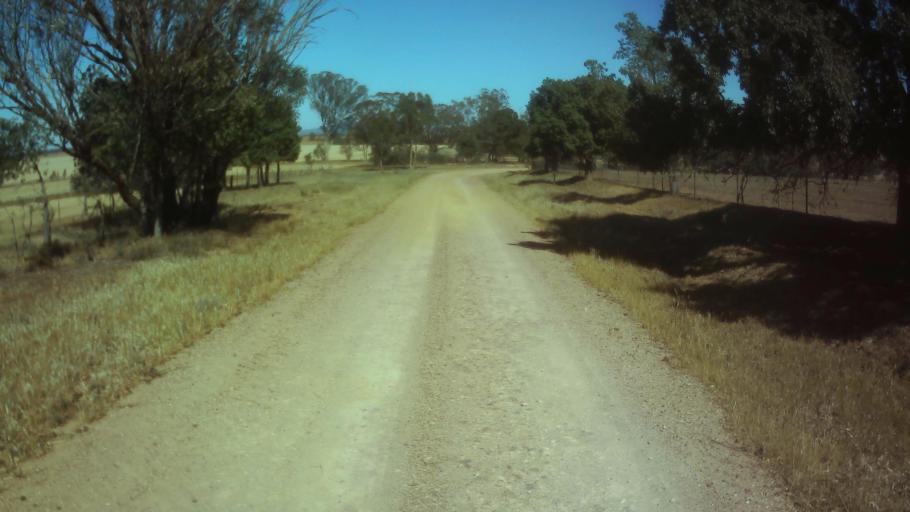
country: AU
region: New South Wales
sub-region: Weddin
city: Grenfell
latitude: -33.9922
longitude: 148.3426
